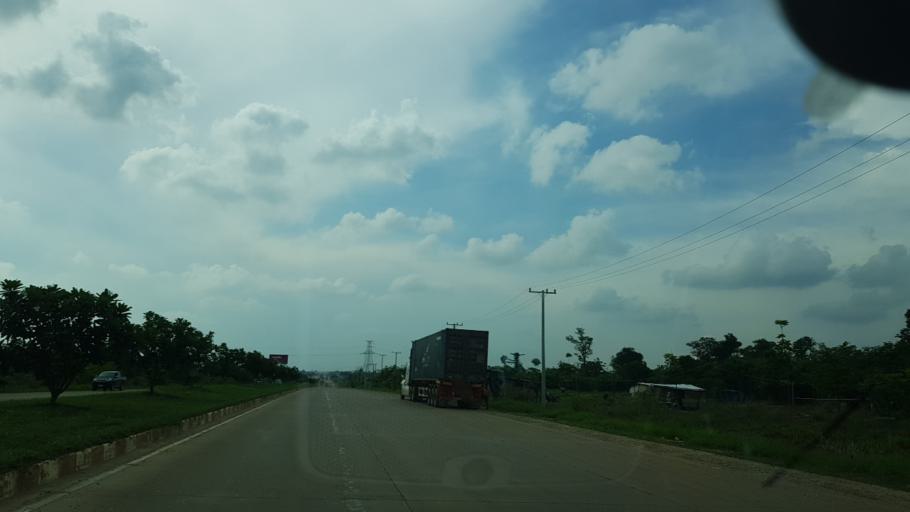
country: TH
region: Nong Khai
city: Nong Khai
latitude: 17.9817
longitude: 102.7186
